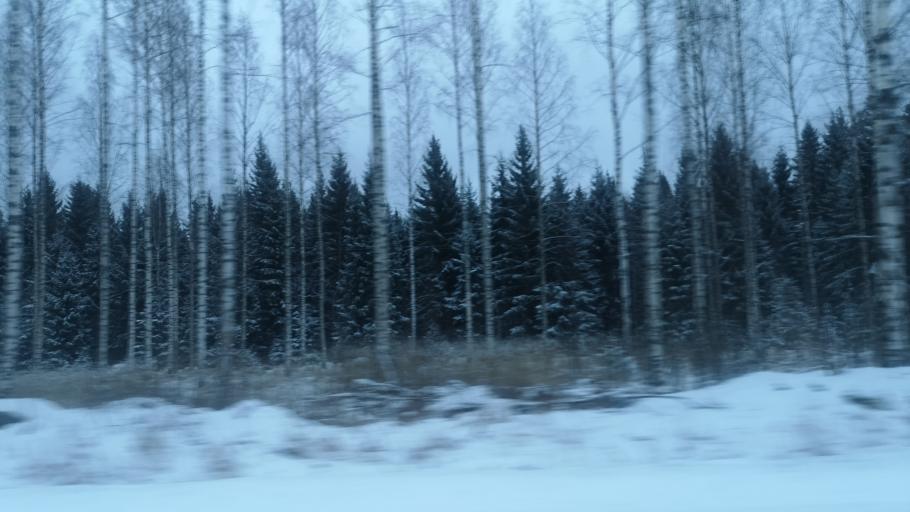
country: FI
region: Southern Savonia
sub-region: Savonlinna
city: Savonlinna
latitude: 62.0068
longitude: 28.7363
